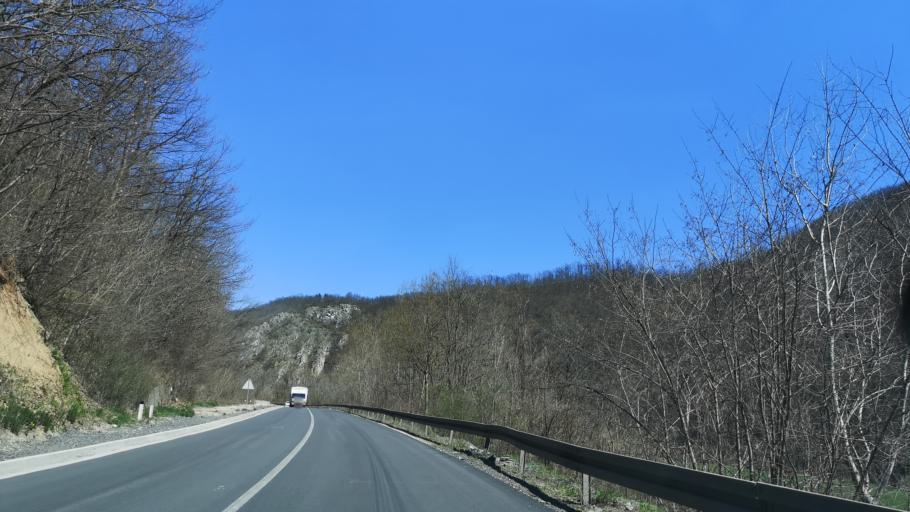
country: RS
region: Central Serbia
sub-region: Moravicki Okrug
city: Lucani
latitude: 43.8849
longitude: 20.1198
